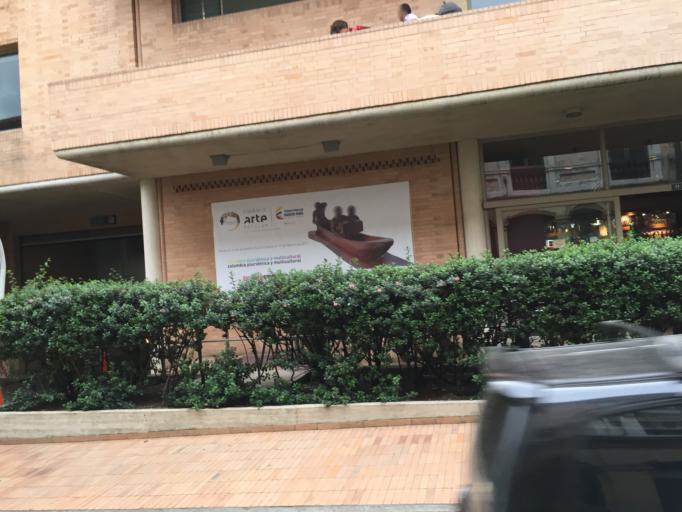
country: CO
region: Bogota D.C.
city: Bogota
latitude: 4.5979
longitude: -74.0743
